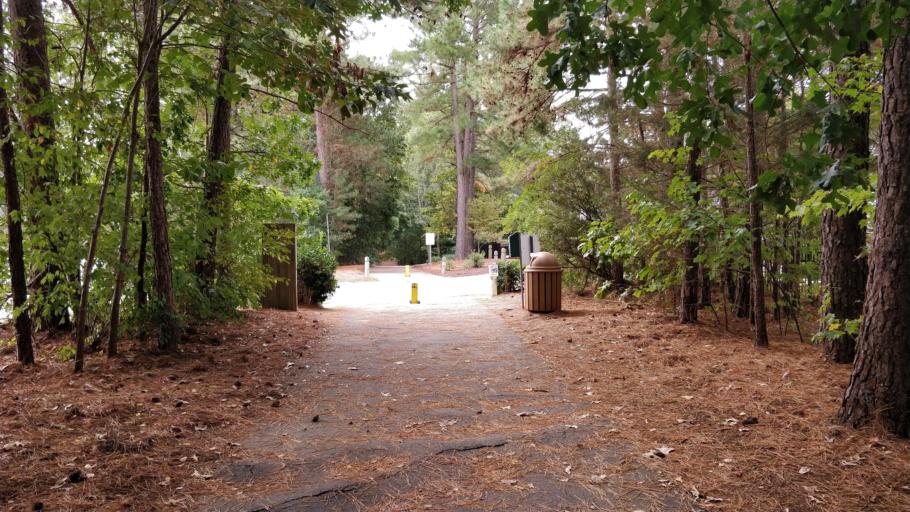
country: US
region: North Carolina
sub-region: Wake County
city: West Raleigh
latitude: 35.9037
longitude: -78.6696
